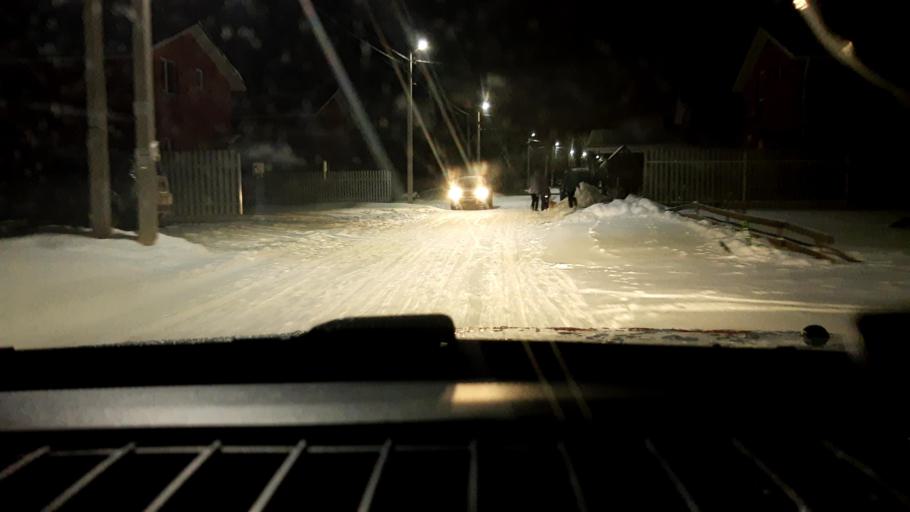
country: RU
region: Nizjnij Novgorod
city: Afonino
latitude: 56.1959
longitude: 44.0687
